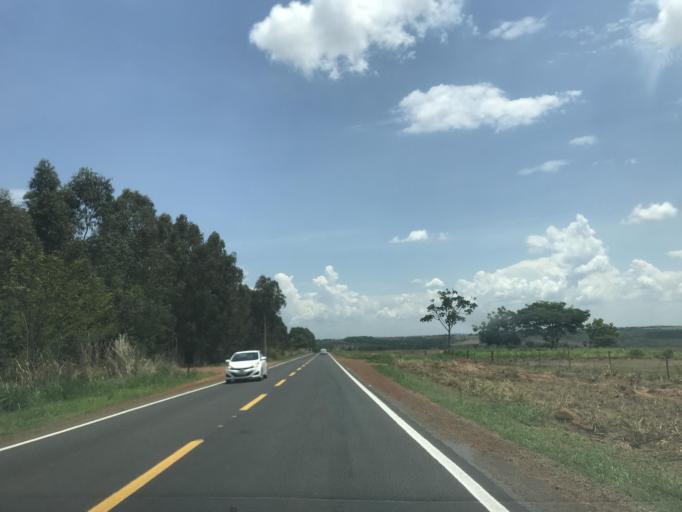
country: BR
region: Goias
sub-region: Bela Vista De Goias
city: Bela Vista de Goias
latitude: -17.1092
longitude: -48.6658
